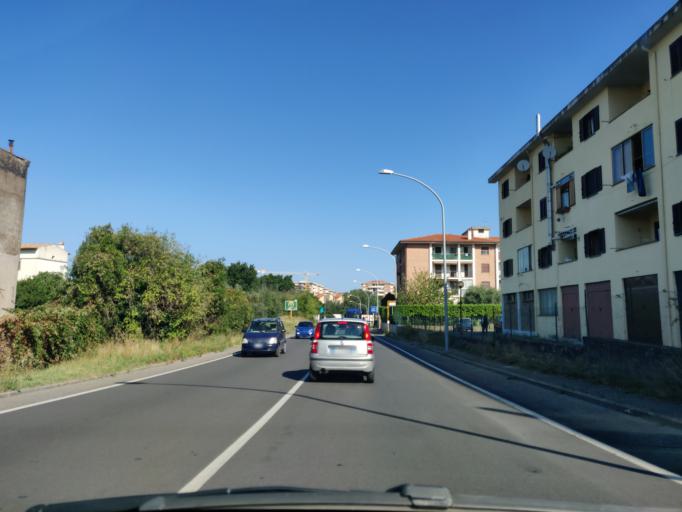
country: IT
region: Latium
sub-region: Provincia di Viterbo
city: Viterbo
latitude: 42.4218
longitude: 12.0943
